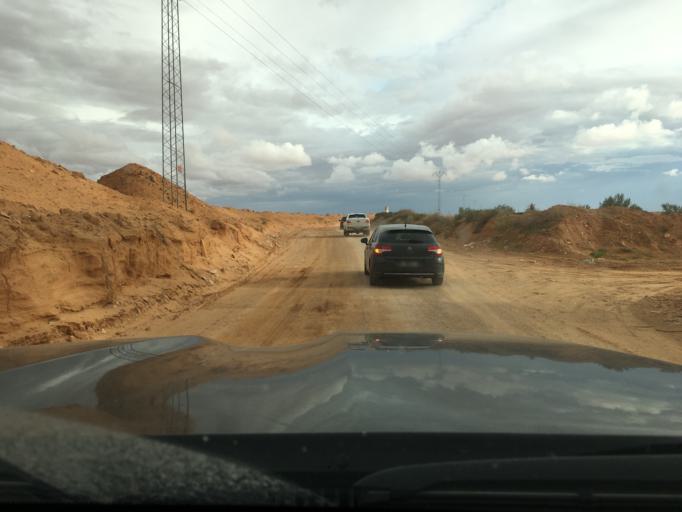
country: TN
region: Madanin
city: Medenine
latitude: 33.2730
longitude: 10.5651
